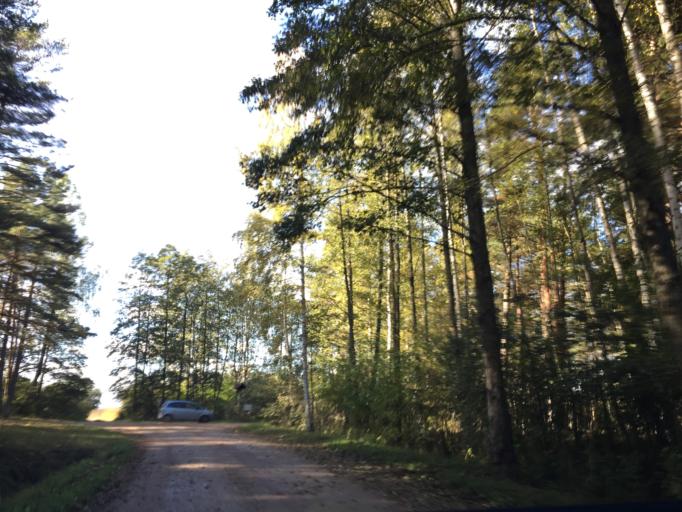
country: LV
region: Mesraga
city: Mersrags
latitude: 57.2581
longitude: 23.1373
